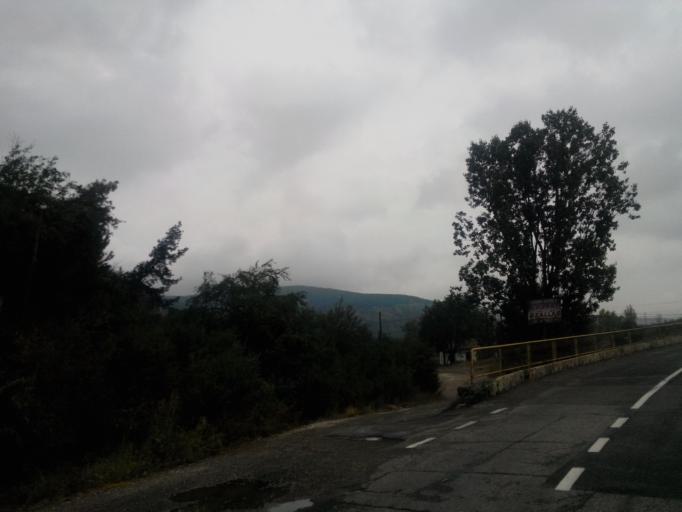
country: RO
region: Cluj
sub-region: Comuna Moldovenesti
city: Moldovenesti
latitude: 46.5111
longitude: 23.6605
